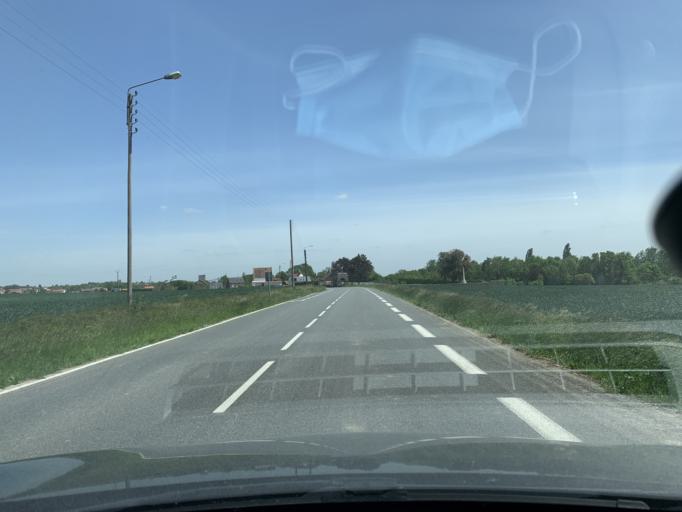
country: FR
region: Nord-Pas-de-Calais
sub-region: Departement du Nord
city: Marcoing
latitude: 50.1184
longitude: 3.1855
